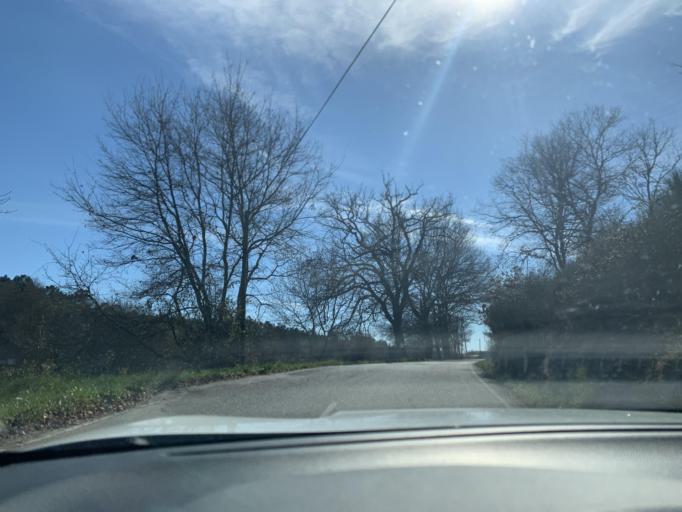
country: PT
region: Viseu
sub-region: Concelho de Tondela
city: Tondela
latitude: 40.5970
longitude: -8.0238
